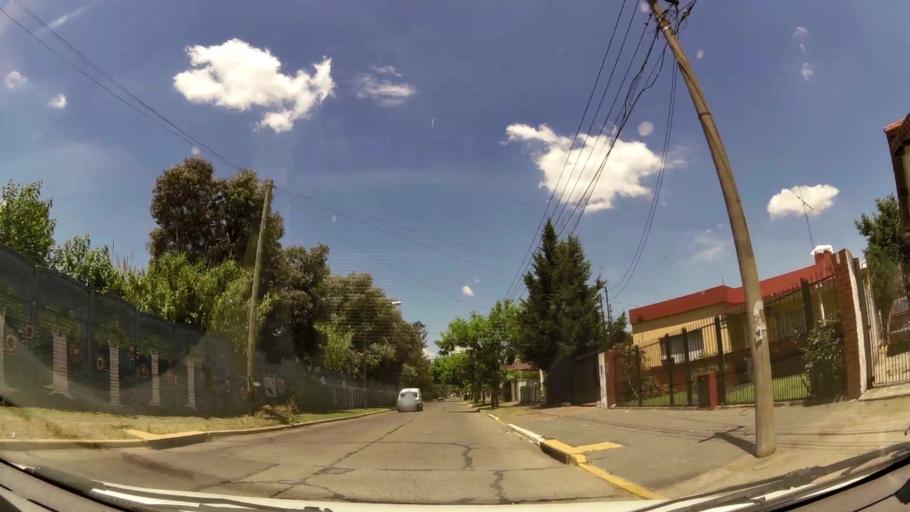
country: AR
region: Buenos Aires
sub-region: Partido de Merlo
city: Merlo
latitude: -34.6604
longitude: -58.7068
